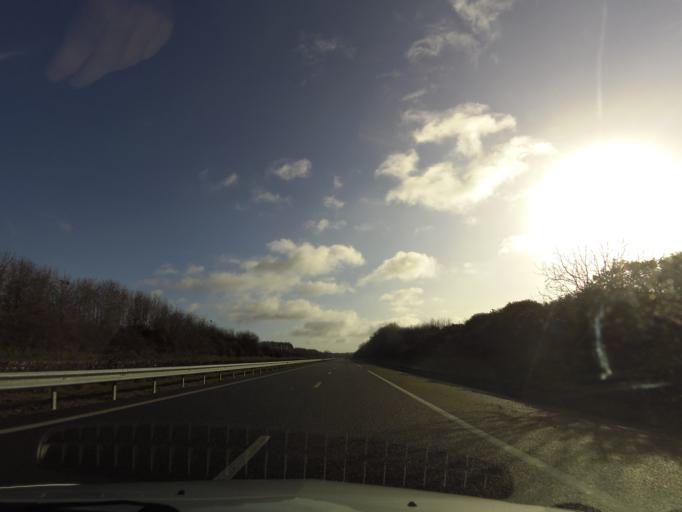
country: FR
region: Brittany
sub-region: Departement d'Ille-et-Vilaine
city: Saint-Sauveur-des-Landes
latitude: 48.3166
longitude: -1.3326
